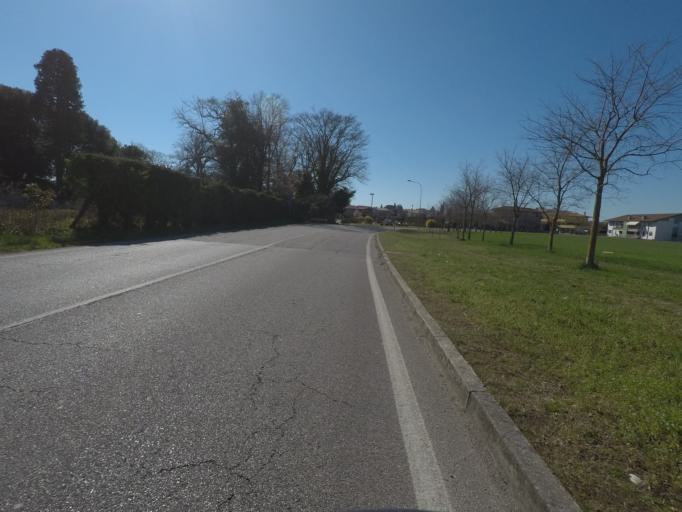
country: IT
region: Friuli Venezia Giulia
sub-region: Provincia di Udine
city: San Giovanni al Natisone
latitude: 45.9829
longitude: 13.4009
